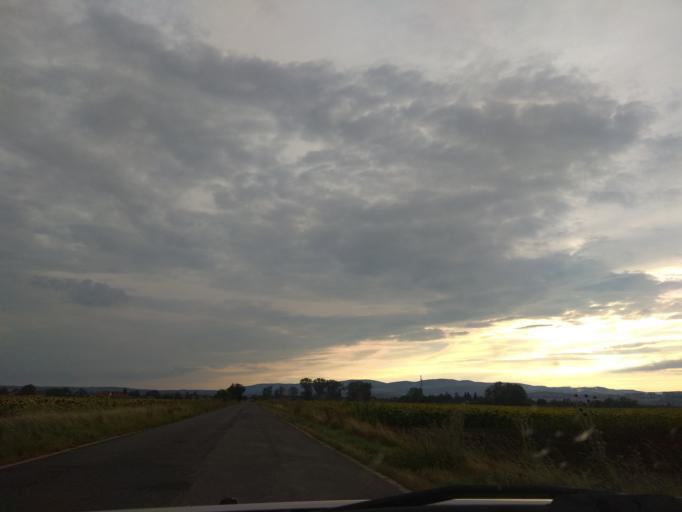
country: HU
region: Borsod-Abauj-Zemplen
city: Felsozsolca
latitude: 48.0786
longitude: 20.8406
